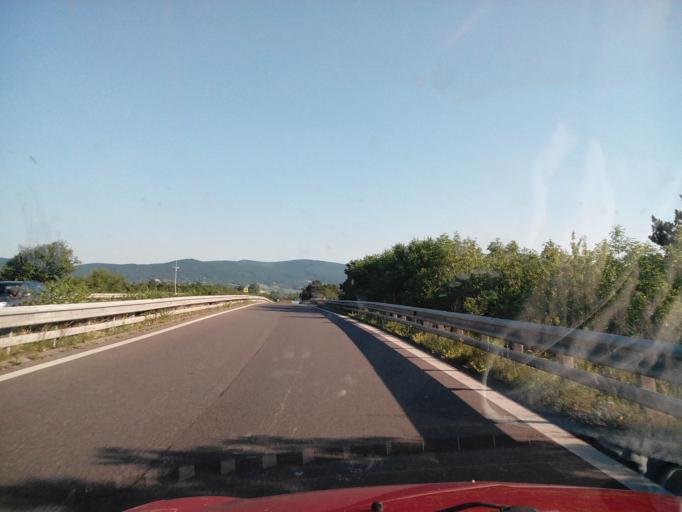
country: AT
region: Lower Austria
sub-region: Politischer Bezirk Baden
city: Traiskirchen
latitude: 47.9856
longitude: 16.2788
